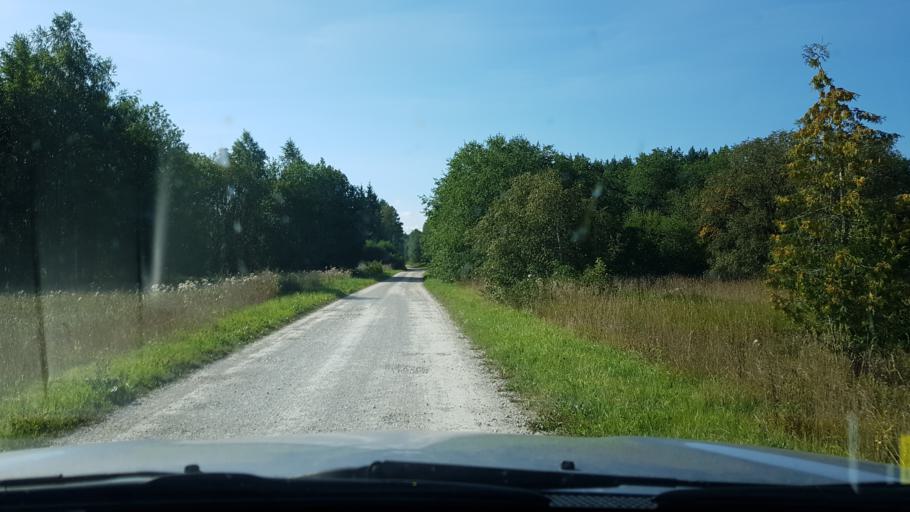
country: EE
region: Ida-Virumaa
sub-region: Toila vald
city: Voka
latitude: 59.3907
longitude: 27.6673
